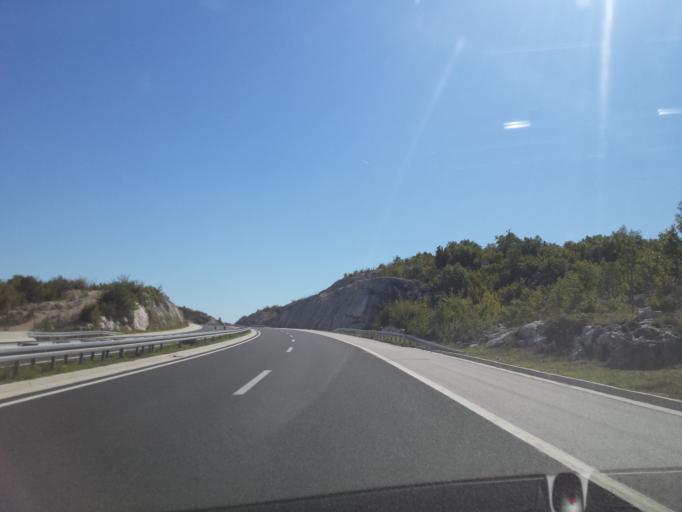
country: HR
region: Splitsko-Dalmatinska
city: Dugopolje
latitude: 43.5878
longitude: 16.6322
